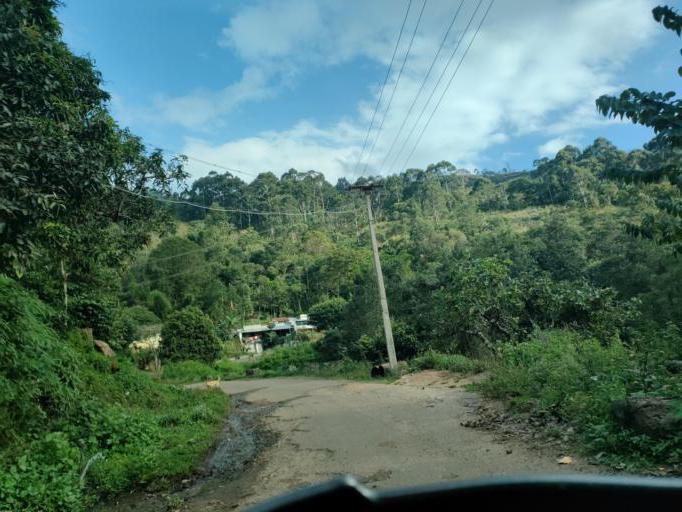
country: IN
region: Tamil Nadu
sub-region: Dindigul
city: Kodaikanal
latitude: 10.2855
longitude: 77.5319
